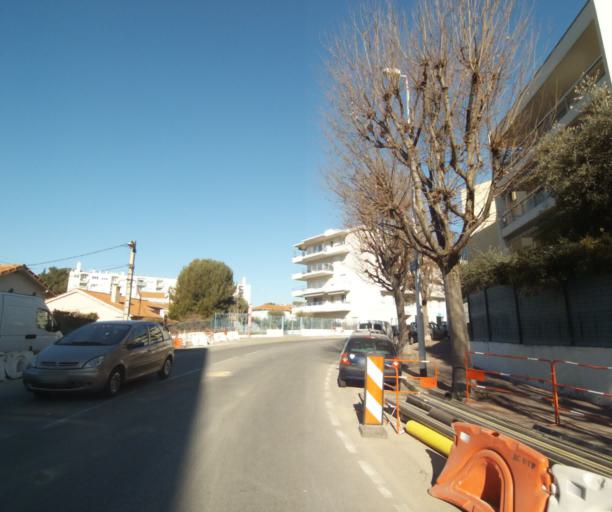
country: FR
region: Provence-Alpes-Cote d'Azur
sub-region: Departement des Alpes-Maritimes
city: Antibes
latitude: 43.5848
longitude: 7.1144
